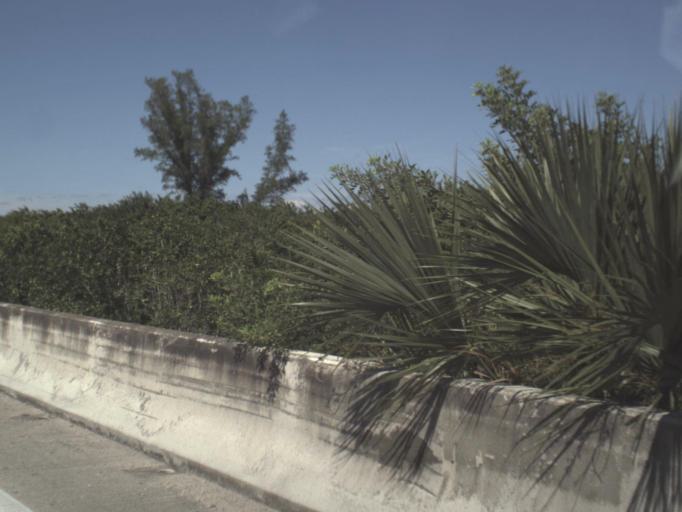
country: US
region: Florida
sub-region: Lee County
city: Tice
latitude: 26.7052
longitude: -81.8037
